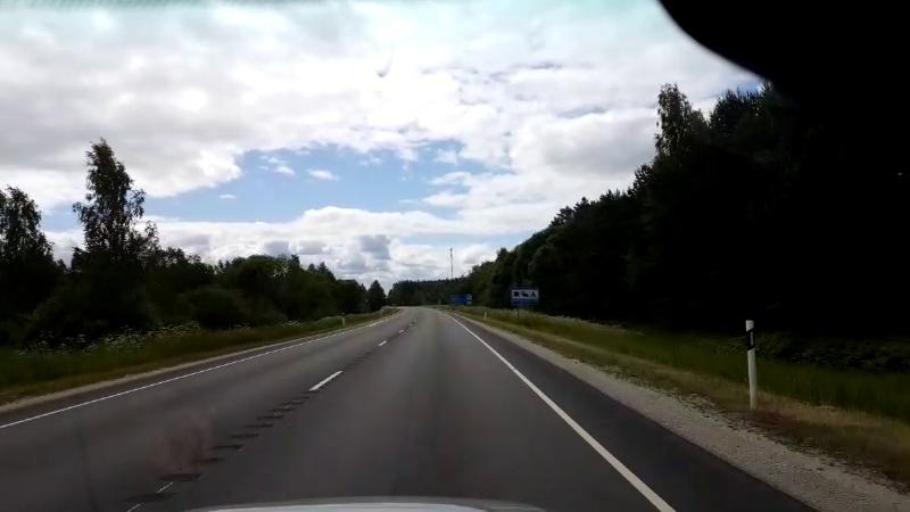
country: LV
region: Salacgrivas
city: Ainazi
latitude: 58.0860
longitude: 24.5087
